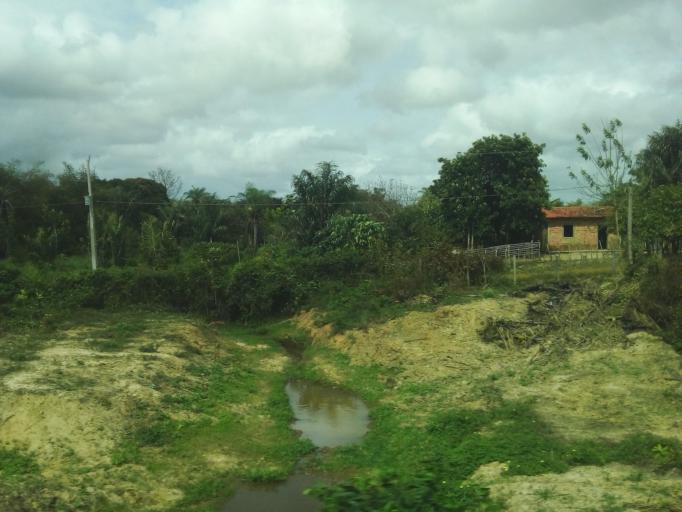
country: BR
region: Maranhao
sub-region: Itapecuru Mirim
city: Itapecuru Mirim
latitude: -3.0467
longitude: -44.3454
